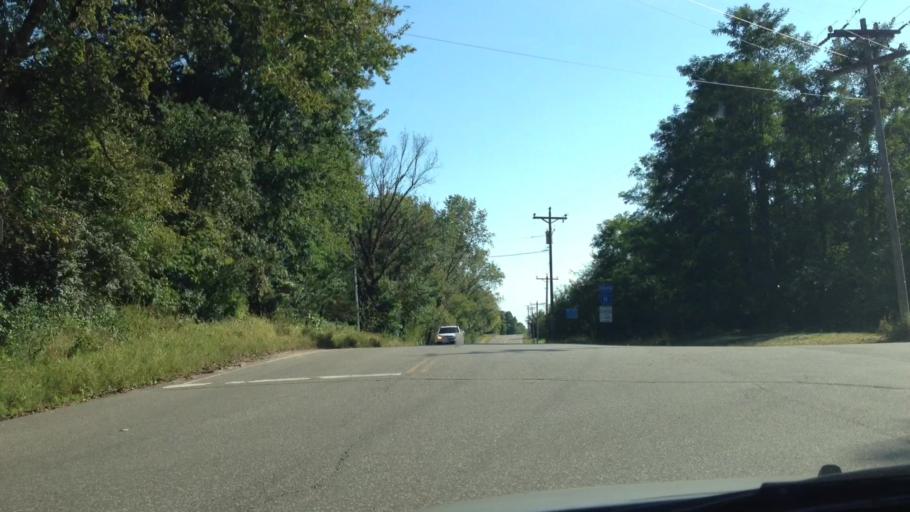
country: US
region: Minnesota
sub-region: Washington County
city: Stillwater
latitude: 45.1002
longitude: -92.8128
